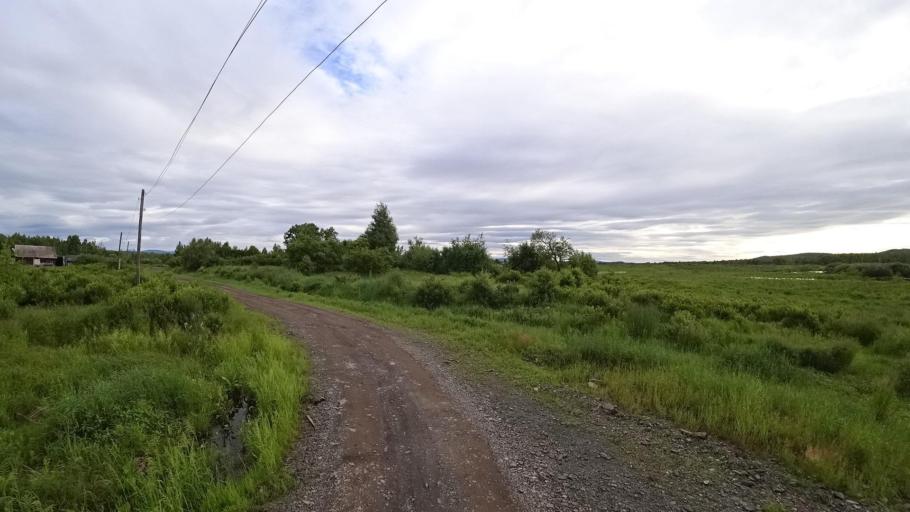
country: RU
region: Khabarovsk Krai
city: Amursk
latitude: 49.8846
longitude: 136.1288
